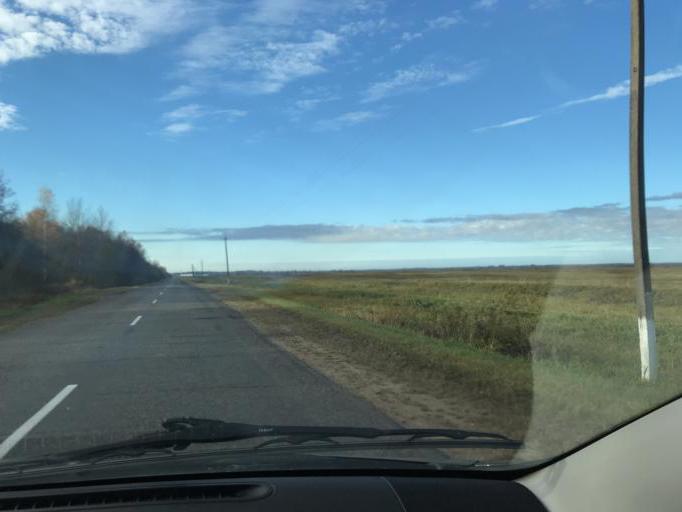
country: BY
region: Vitebsk
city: Haradok
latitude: 55.3896
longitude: 29.6696
